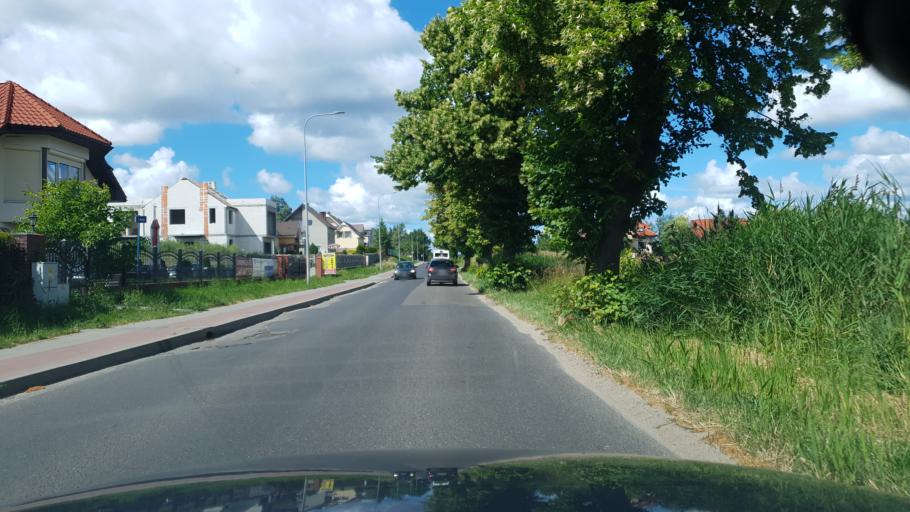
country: PL
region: Pomeranian Voivodeship
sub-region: Powiat pucki
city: Mosty
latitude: 54.6264
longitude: 18.4967
